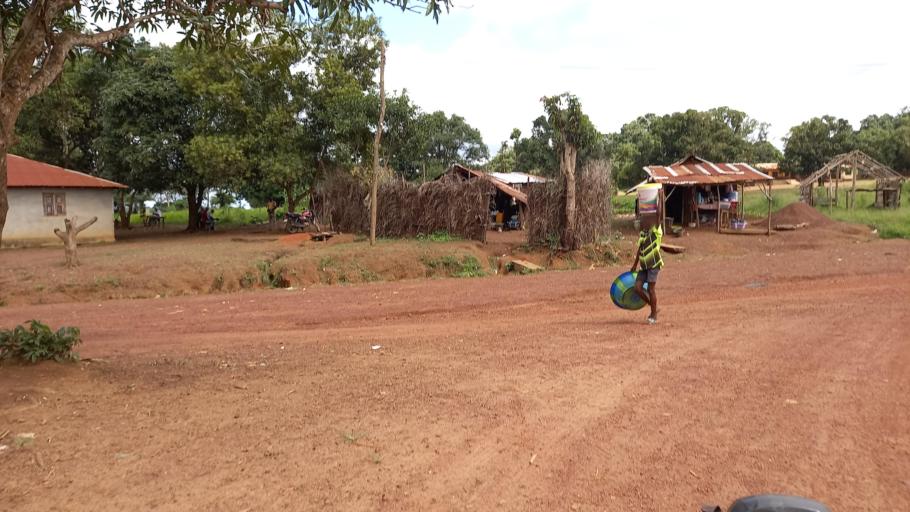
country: SL
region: Northern Province
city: Kamakwie
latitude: 9.5018
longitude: -12.2370
